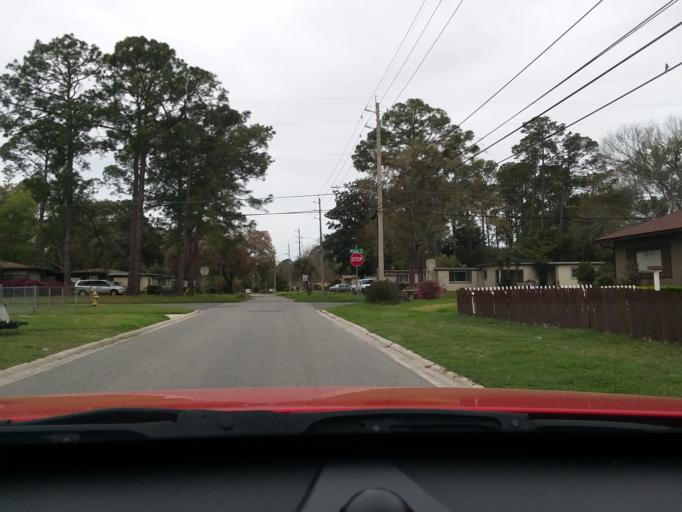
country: US
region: Florida
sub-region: Duval County
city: Jacksonville
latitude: 30.2840
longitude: -81.7320
